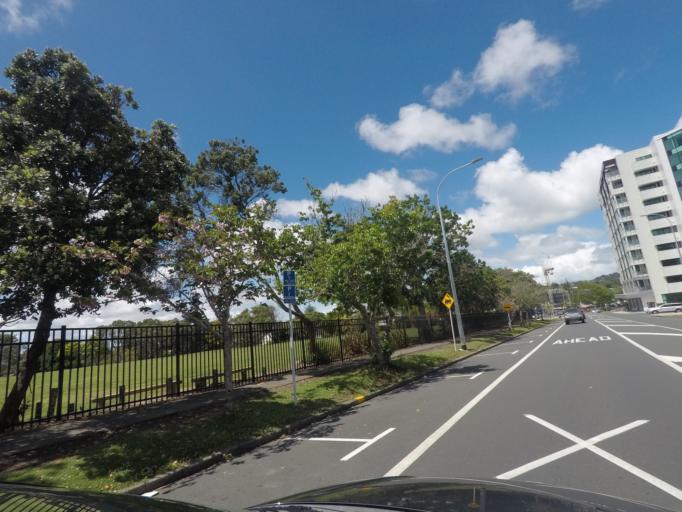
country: NZ
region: Auckland
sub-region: Auckland
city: Waitakere
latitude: -36.9086
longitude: 174.6519
